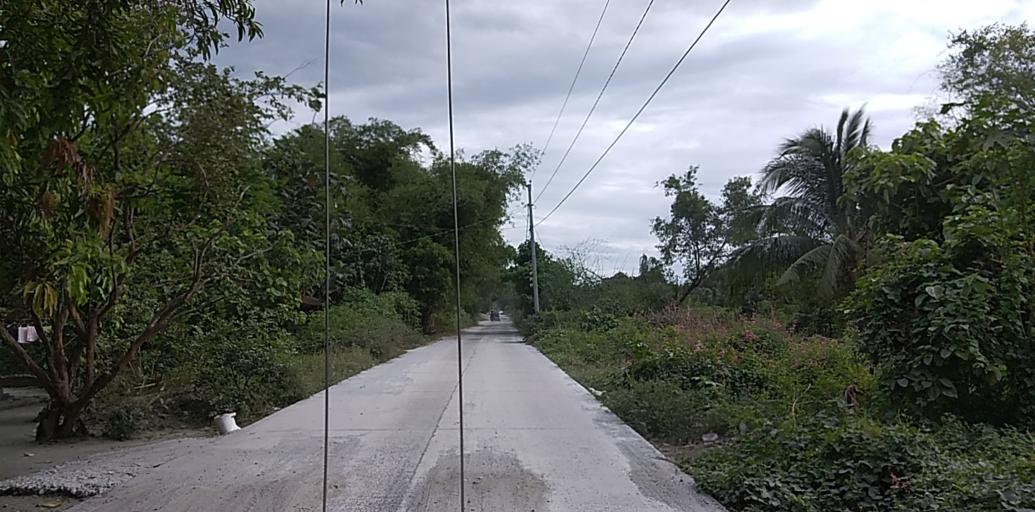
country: PH
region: Central Luzon
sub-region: Province of Pampanga
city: Pulung Santol
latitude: 15.0553
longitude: 120.5590
